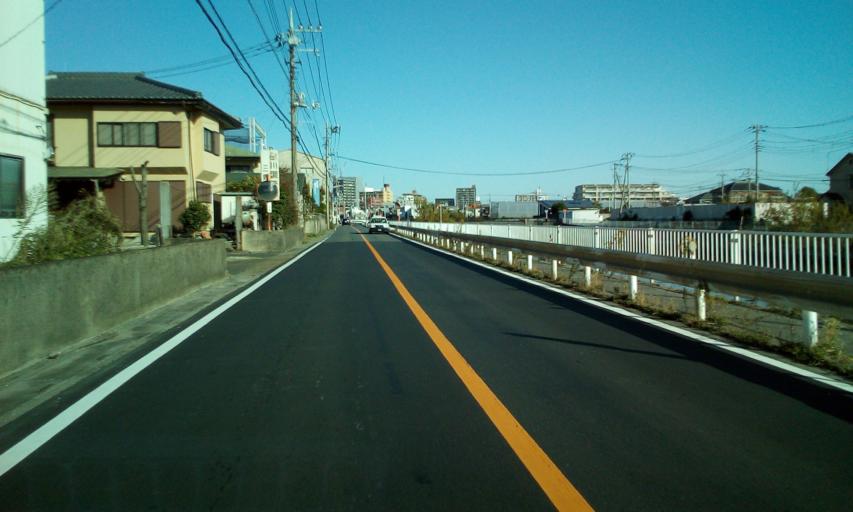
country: JP
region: Chiba
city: Nagareyama
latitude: 35.8366
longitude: 139.8839
